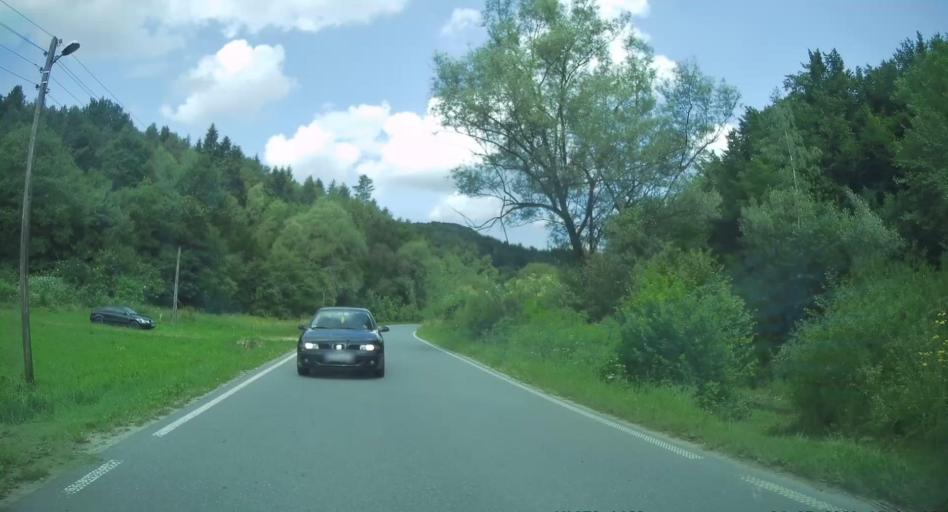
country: PL
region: Lesser Poland Voivodeship
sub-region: Powiat nowosadecki
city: Korzenna
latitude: 49.7411
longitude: 20.7692
